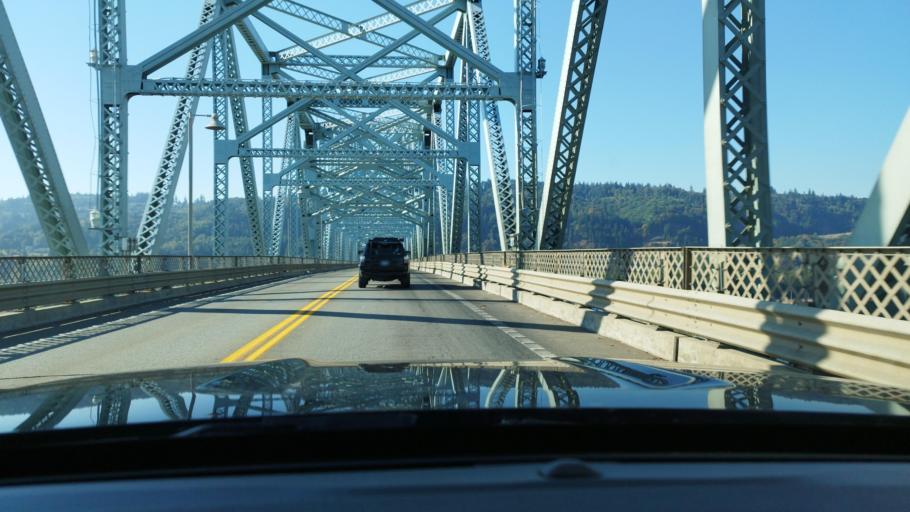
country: US
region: Oregon
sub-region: Columbia County
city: Rainier
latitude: 46.1049
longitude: -122.9619
